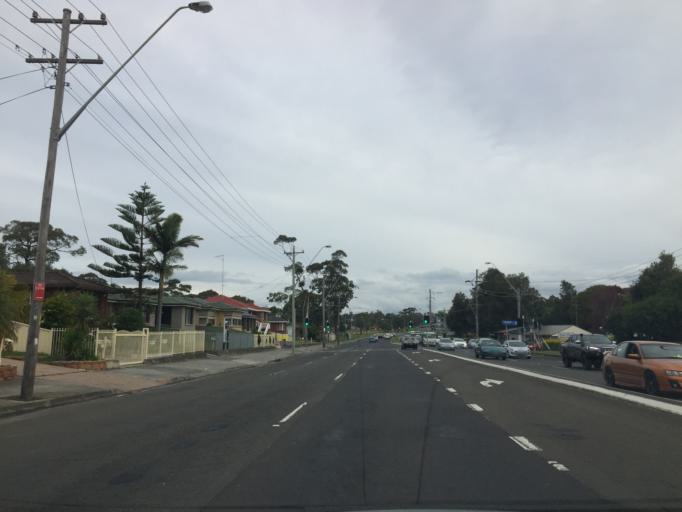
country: AU
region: New South Wales
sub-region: Shellharbour
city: Barrack Heights
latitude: -34.5579
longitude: 150.8449
